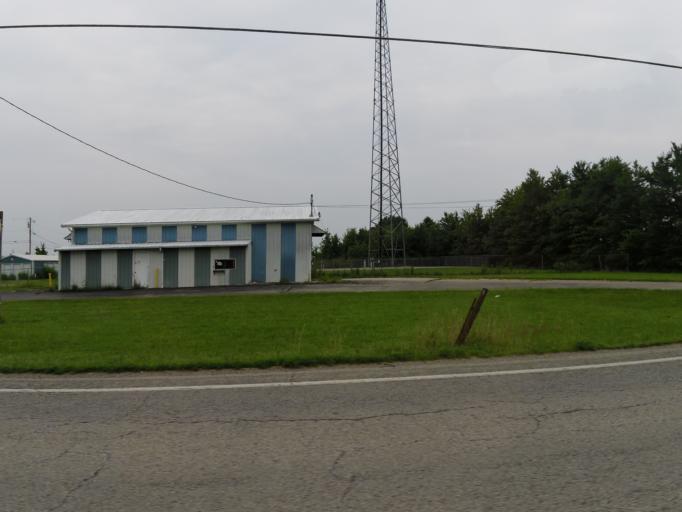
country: US
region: Ohio
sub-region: Brown County
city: Mount Orab
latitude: 39.1169
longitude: -83.9328
